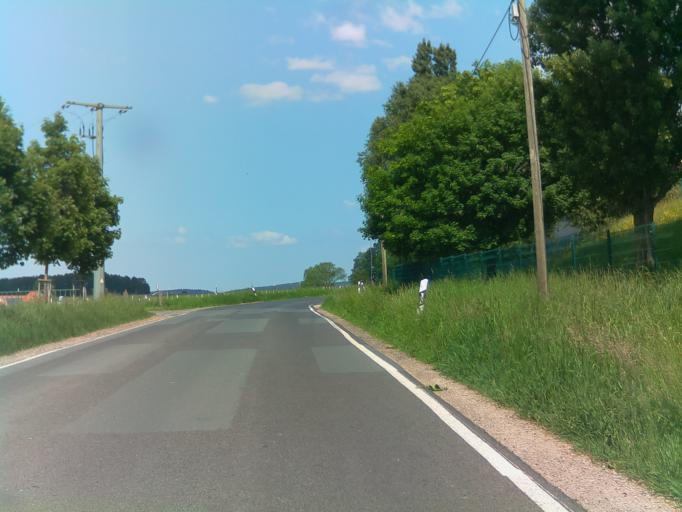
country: DE
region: Thuringia
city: Dermbach
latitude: 50.7161
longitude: 10.1448
